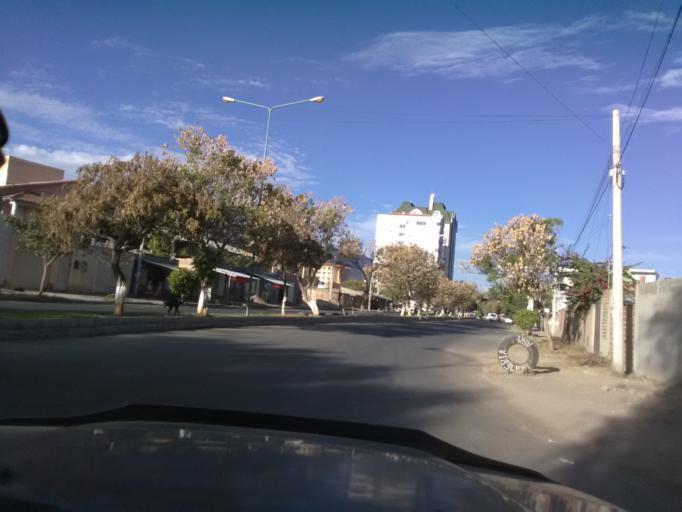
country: BO
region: Cochabamba
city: Cochabamba
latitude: -17.3709
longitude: -66.1904
